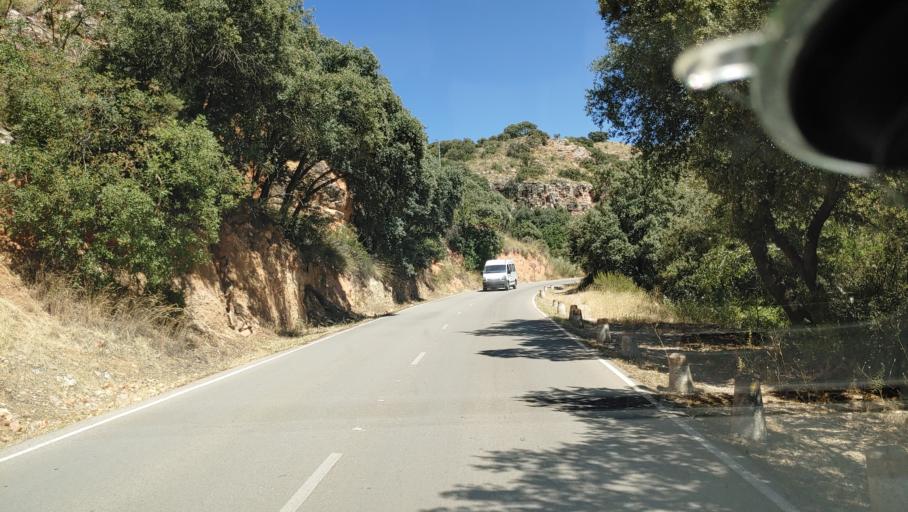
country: ES
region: Castille-La Mancha
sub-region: Provincia de Ciudad Real
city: Ruidera
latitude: 38.9608
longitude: -2.8618
